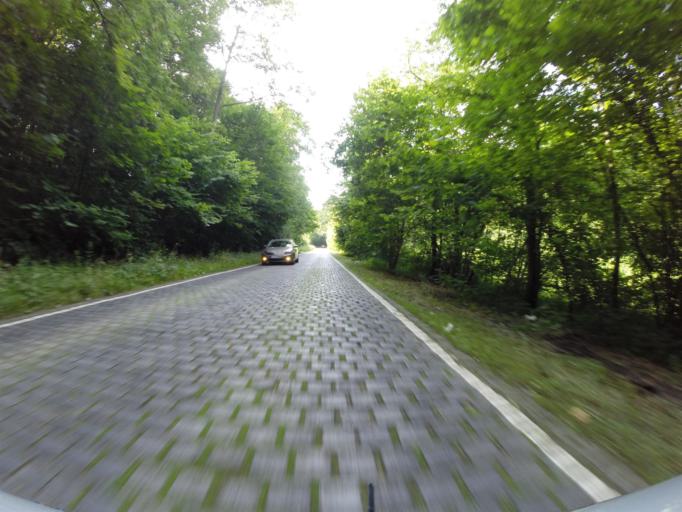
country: DE
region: Thuringia
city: Jena
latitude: 50.9565
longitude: 11.5950
